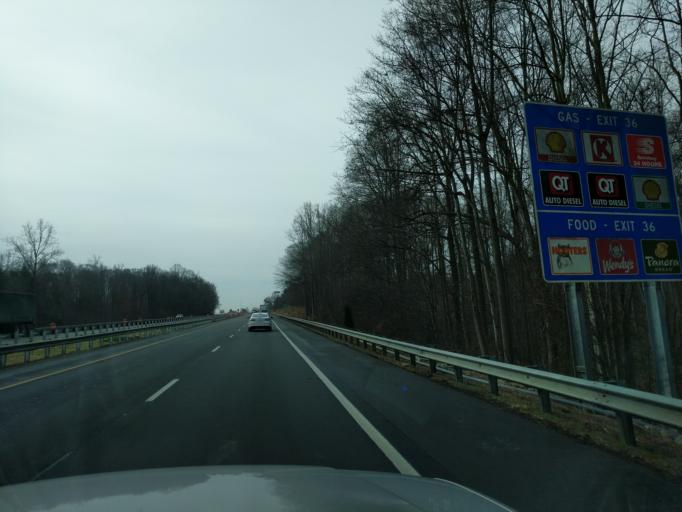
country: US
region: North Carolina
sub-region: Iredell County
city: Mooresville
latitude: 35.6029
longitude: -80.8595
